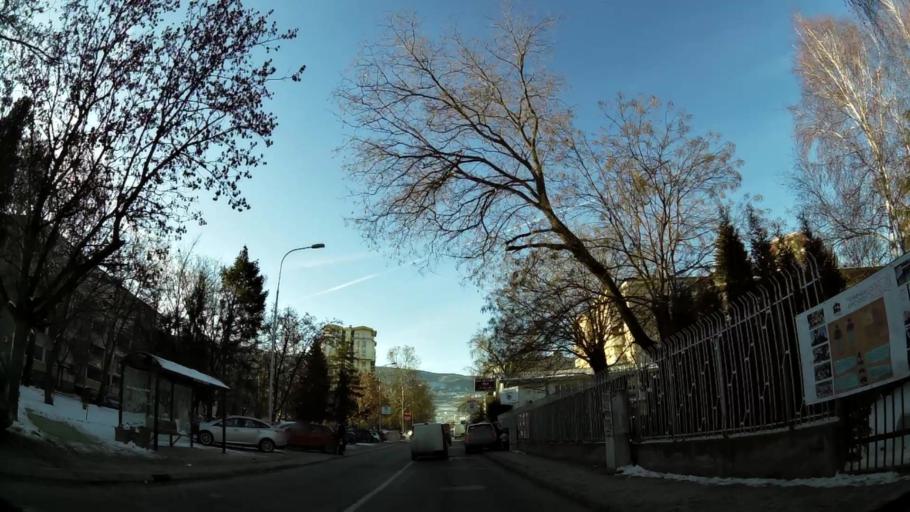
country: MK
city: Krushopek
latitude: 42.0070
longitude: 21.3835
